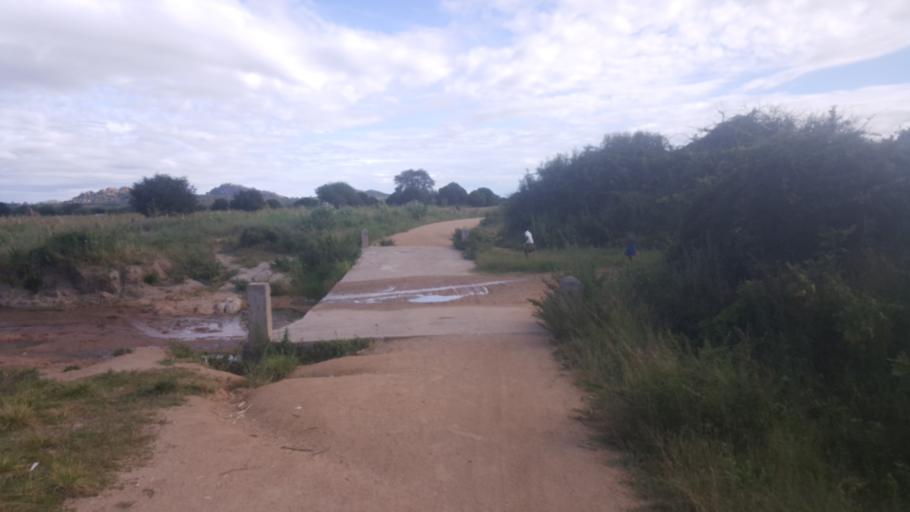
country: TZ
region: Dodoma
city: Dodoma
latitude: -6.0935
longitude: 35.5281
